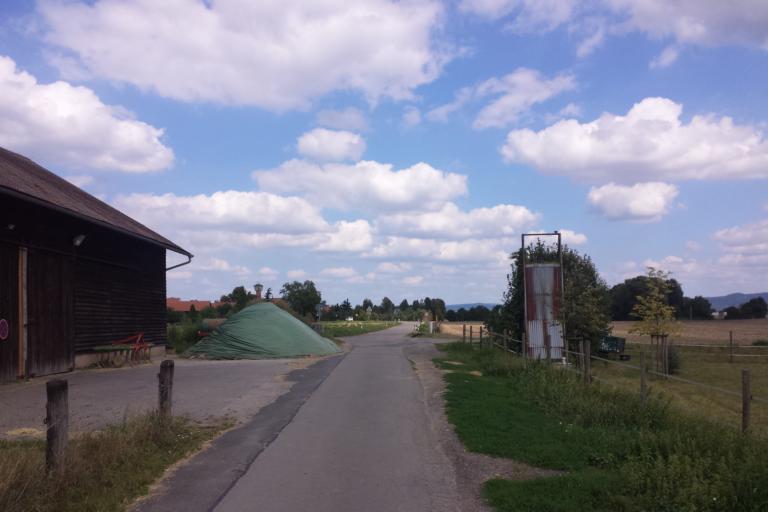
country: DE
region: Baden-Wuerttemberg
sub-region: Karlsruhe Region
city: Heddesheim
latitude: 49.5084
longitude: 8.5748
